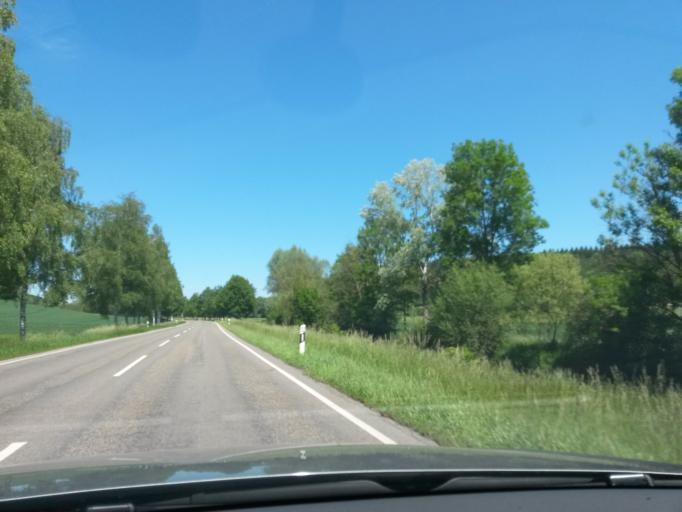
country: DE
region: Baden-Wuerttemberg
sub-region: Regierungsbezirk Stuttgart
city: Weil der Stadt
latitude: 48.7322
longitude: 8.8793
